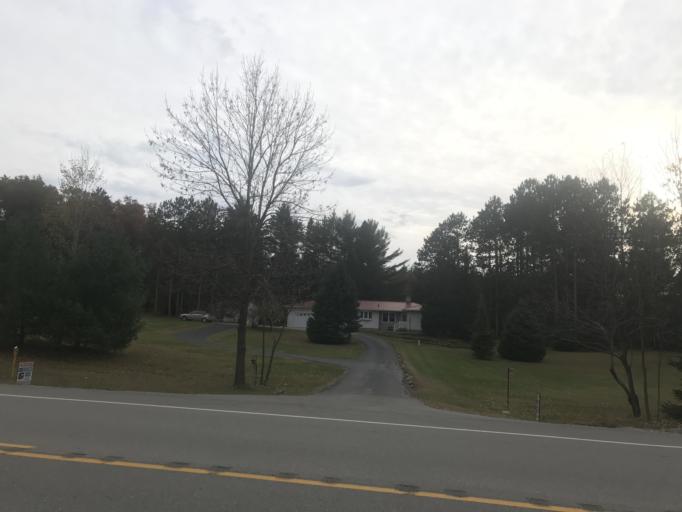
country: US
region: Wisconsin
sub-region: Marinette County
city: Marinette
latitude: 45.1570
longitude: -87.7150
